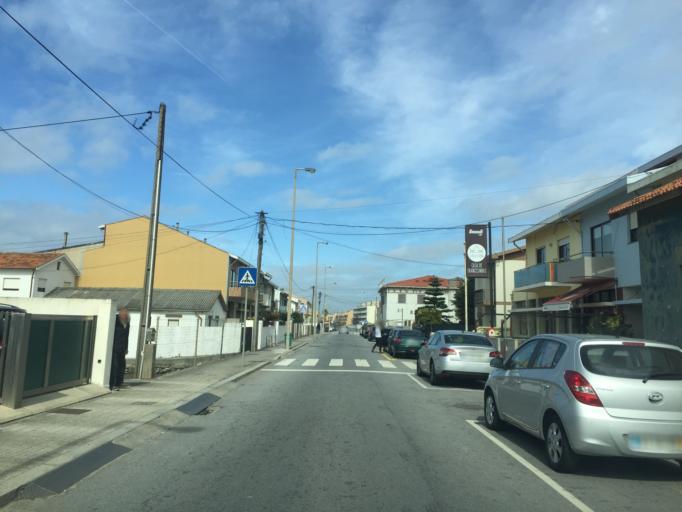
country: PT
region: Porto
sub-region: Matosinhos
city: Lavra
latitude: 41.2415
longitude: -8.7226
